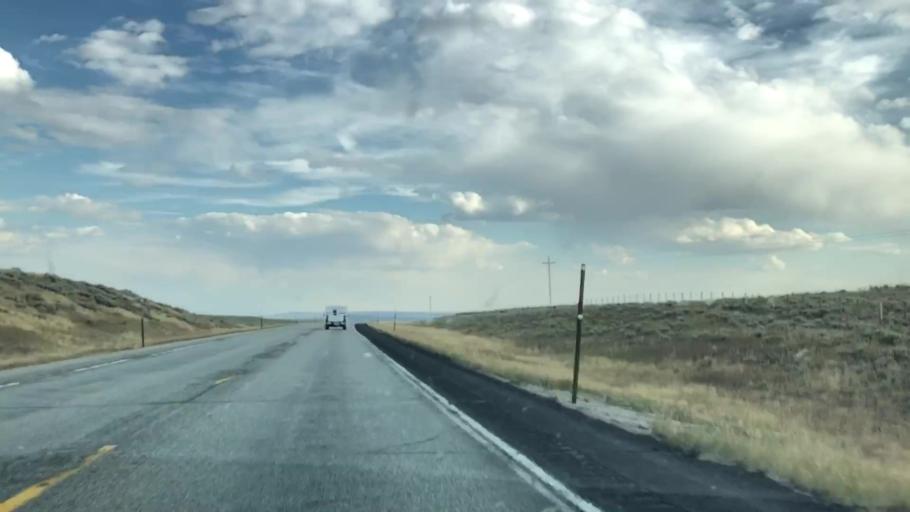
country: US
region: Wyoming
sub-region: Sublette County
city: Pinedale
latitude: 43.0571
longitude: -110.1566
